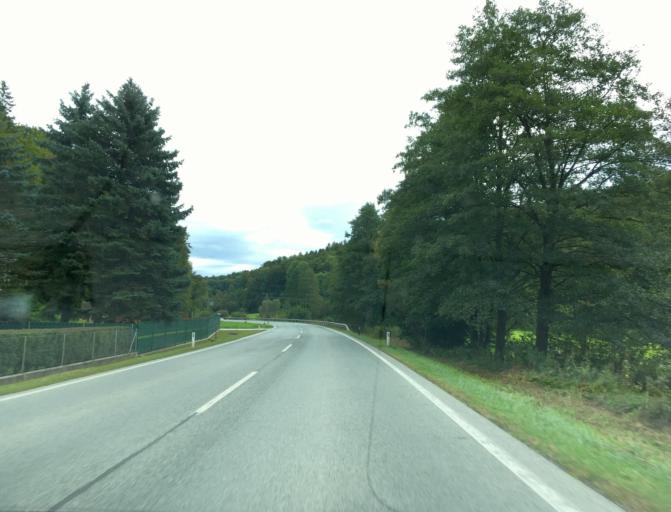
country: AT
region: Lower Austria
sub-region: Politischer Bezirk Wiener Neustadt
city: Bad Schonau
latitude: 47.5005
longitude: 16.2095
